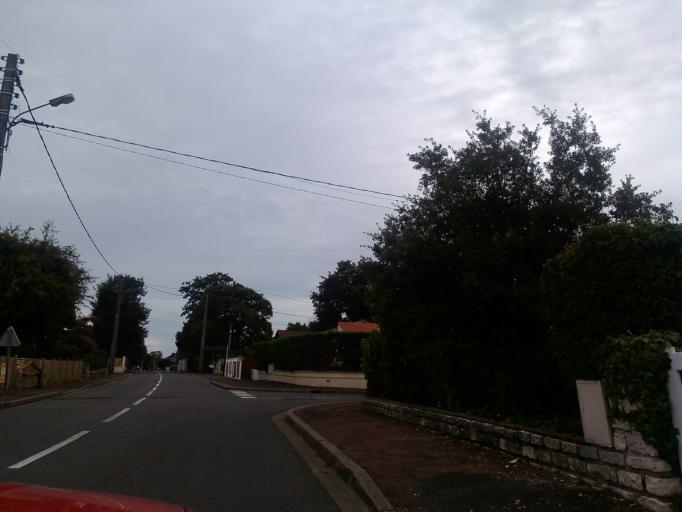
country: FR
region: Poitou-Charentes
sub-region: Departement de la Charente-Maritime
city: Vaux-sur-Mer
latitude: 45.6383
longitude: -1.0685
